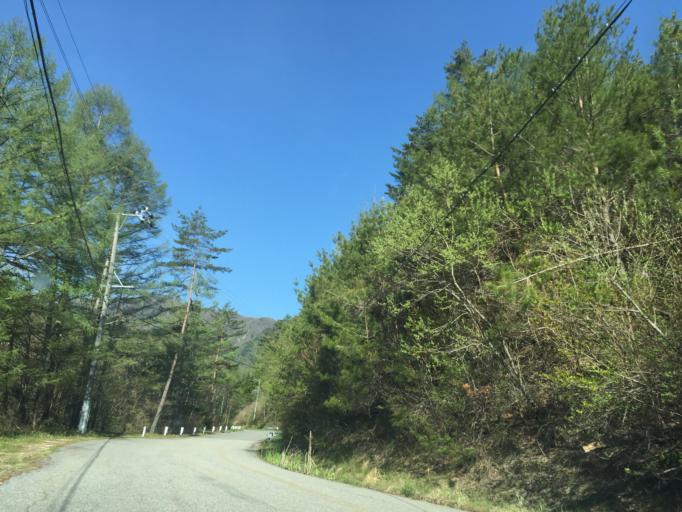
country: JP
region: Nagano
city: Iida
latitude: 35.4067
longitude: 137.6838
